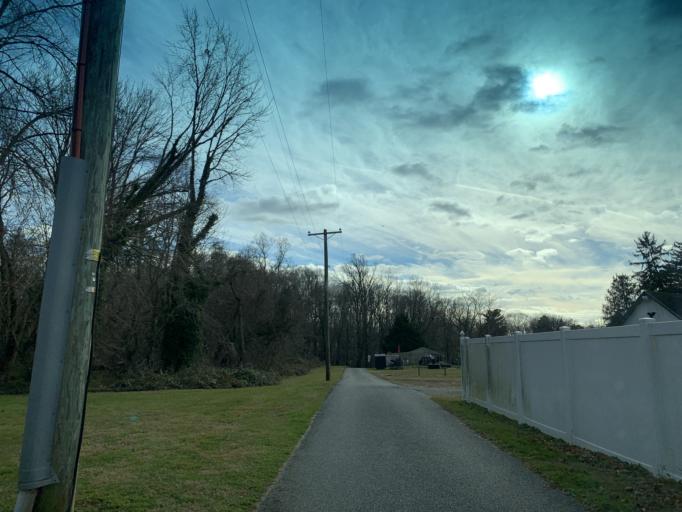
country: US
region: Maryland
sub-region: Harford County
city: Aberdeen Proving Ground
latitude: 39.3665
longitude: -76.0619
